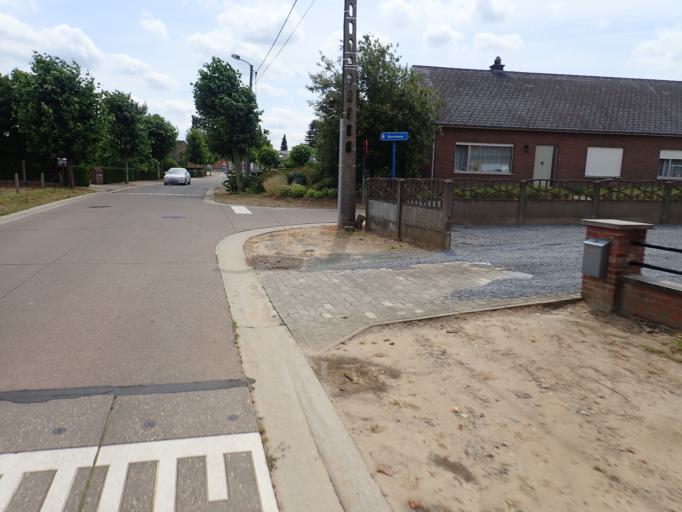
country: BE
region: Flanders
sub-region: Provincie Vlaams-Brabant
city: Keerbergen
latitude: 51.0084
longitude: 4.6300
